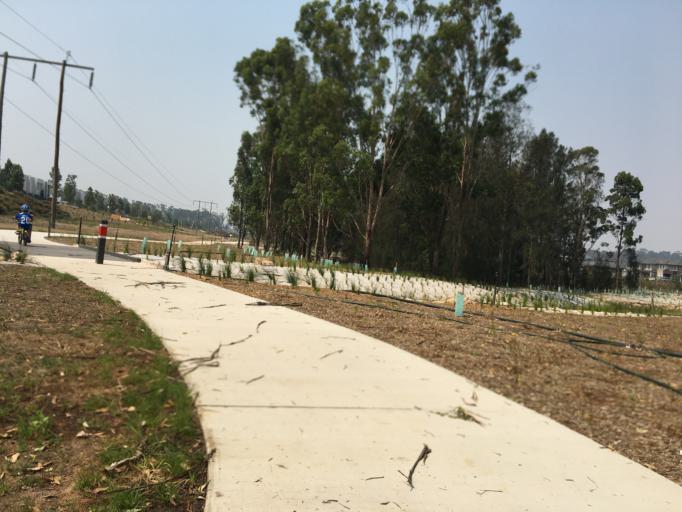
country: AU
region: New South Wales
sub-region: Campbelltown Municipality
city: Denham Court
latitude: -33.9766
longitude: 150.8142
